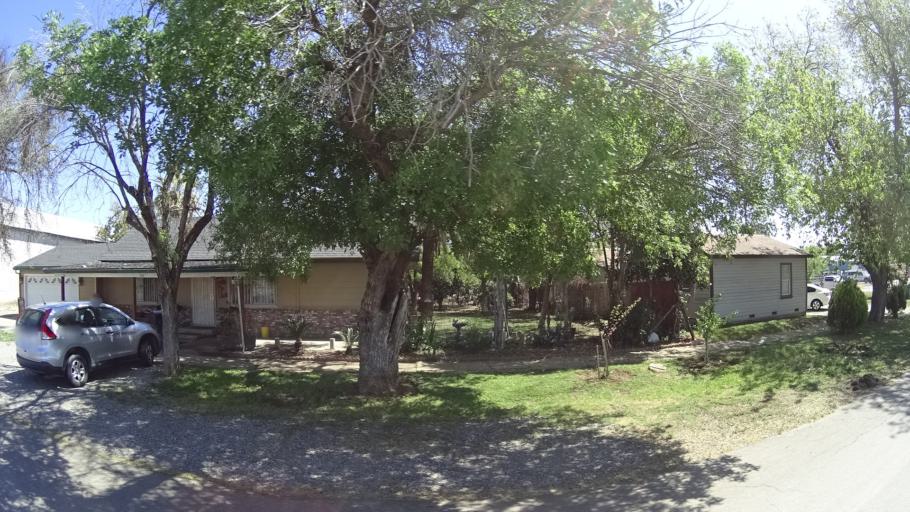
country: US
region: California
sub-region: Glenn County
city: Willows
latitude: 39.5196
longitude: -122.1923
